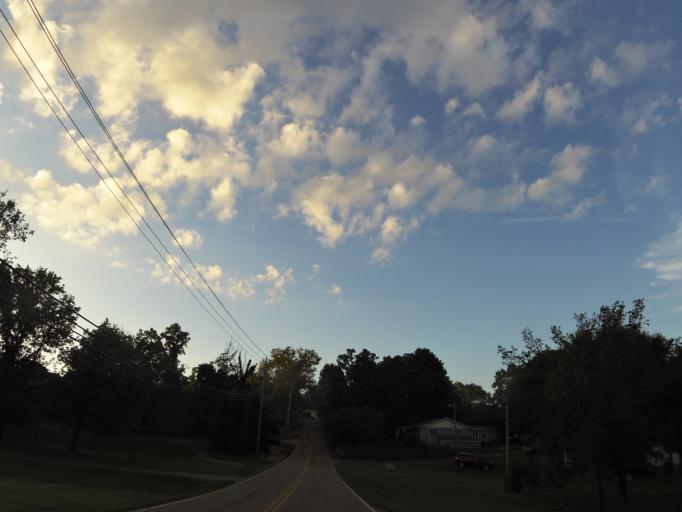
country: US
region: Tennessee
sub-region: Knox County
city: Farragut
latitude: 35.9093
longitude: -84.1709
